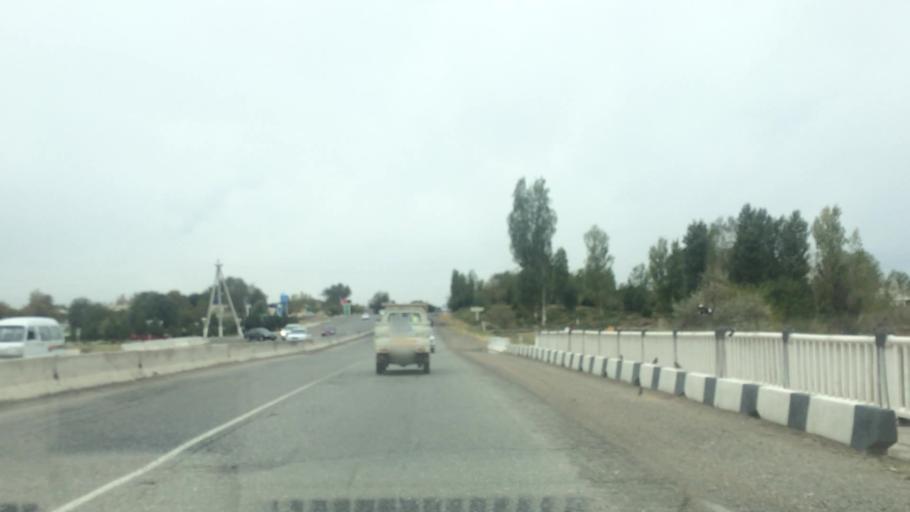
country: UZ
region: Samarqand
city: Bulung'ur
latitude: 39.7732
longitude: 67.2797
